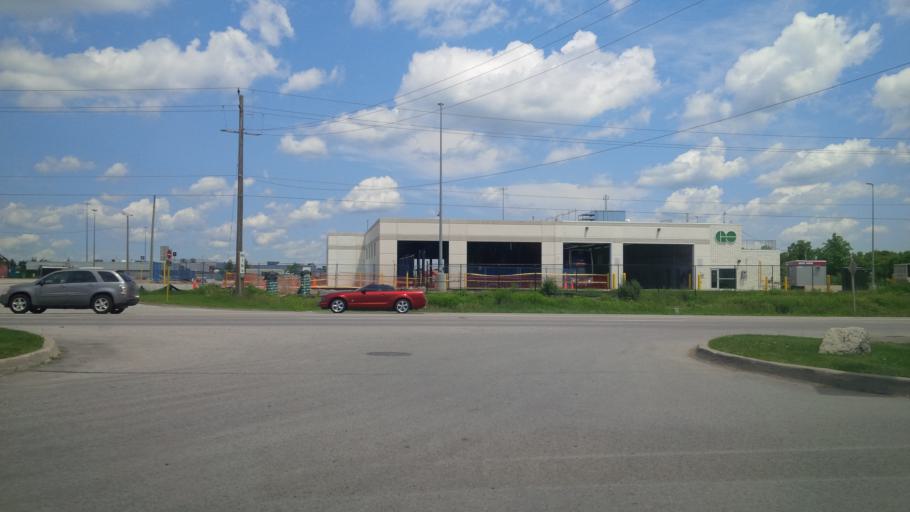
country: CA
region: Ontario
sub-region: Wellington County
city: Guelph
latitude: 43.4595
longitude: -80.1339
